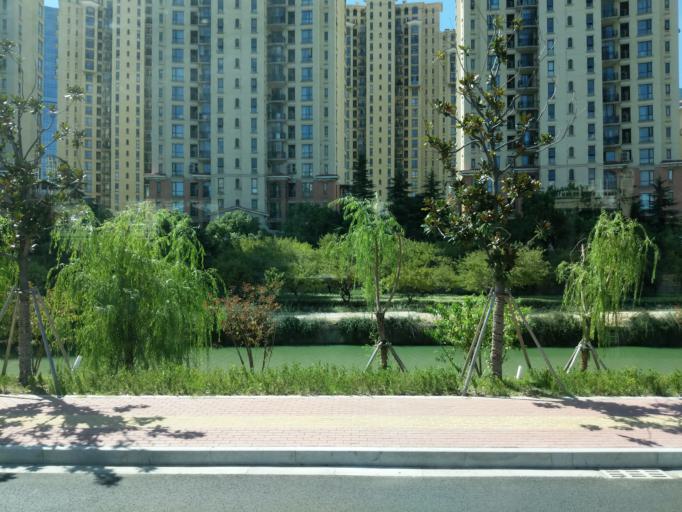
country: CN
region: Jiangsu Sheng
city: Weiting
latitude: 31.3242
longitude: 120.6718
